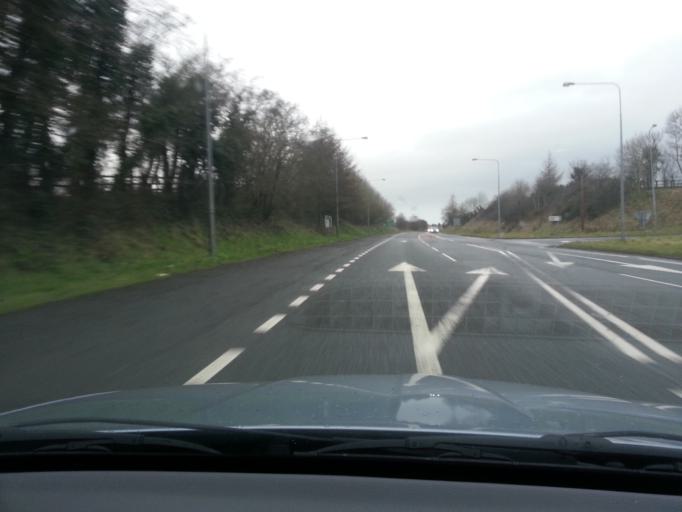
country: GB
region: Northern Ireland
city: Lisnaskea
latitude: 54.2977
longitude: -7.4675
